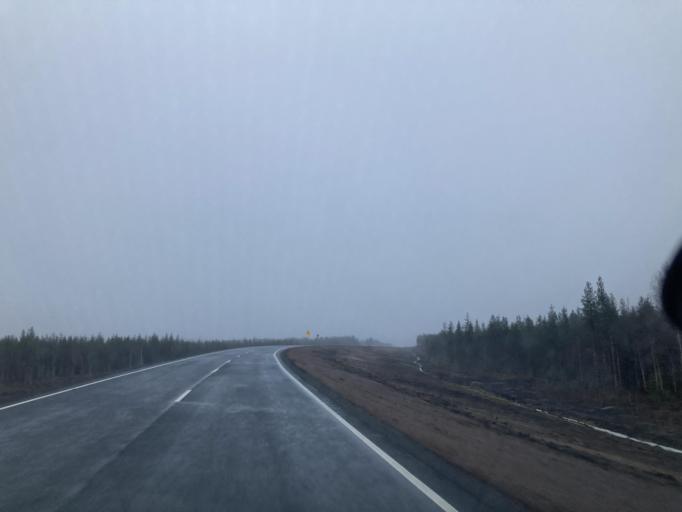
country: FI
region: Lapland
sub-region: Rovaniemi
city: Rovaniemi
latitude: 66.5878
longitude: 25.8010
